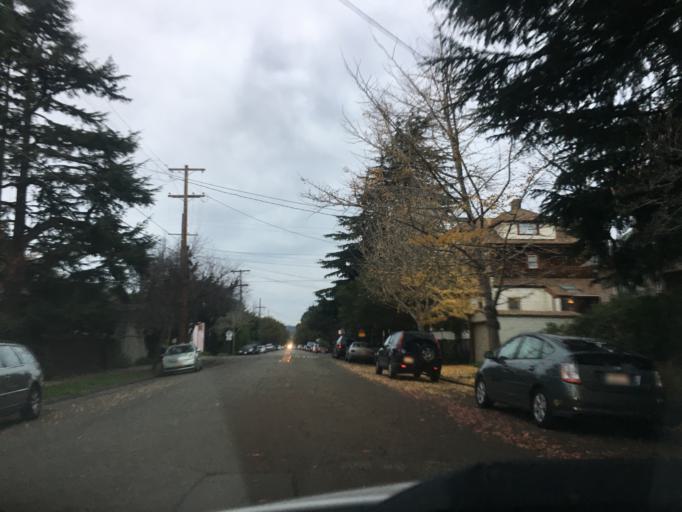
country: US
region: California
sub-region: Alameda County
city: Berkeley
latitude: 37.8638
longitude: -122.2779
